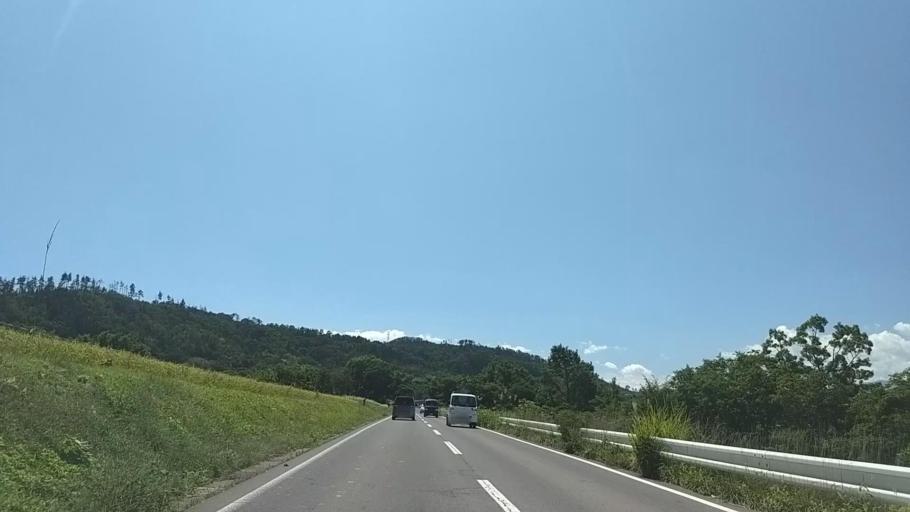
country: JP
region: Nagano
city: Kamimaruko
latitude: 36.3504
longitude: 138.2919
